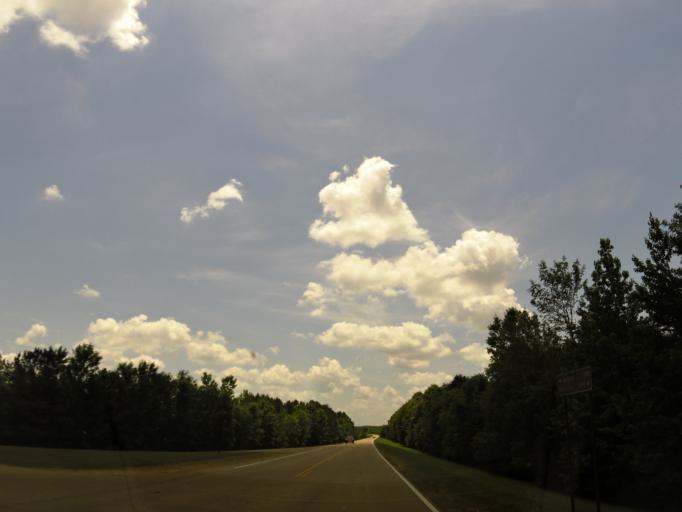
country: US
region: Mississippi
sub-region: Lee County
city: Verona
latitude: 34.2350
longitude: -88.7670
